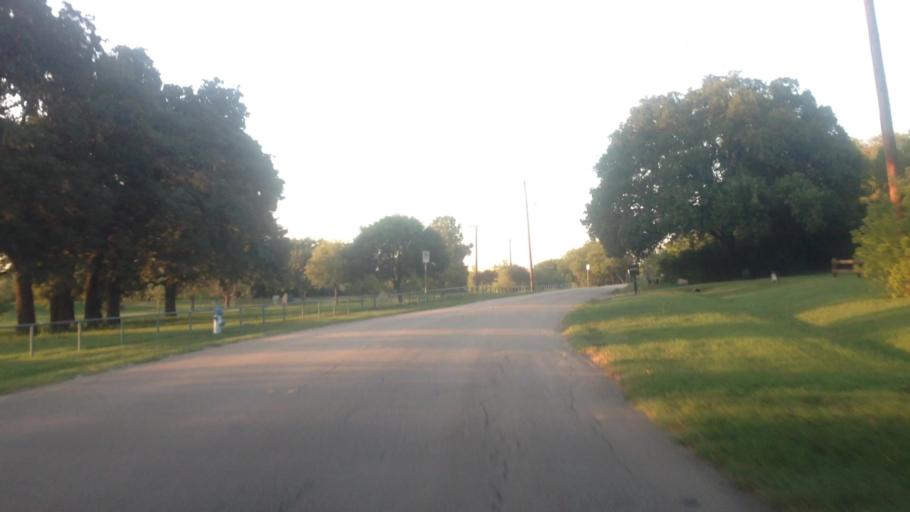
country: US
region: Texas
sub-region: Denton County
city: Denton
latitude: 33.2010
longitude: -97.1546
